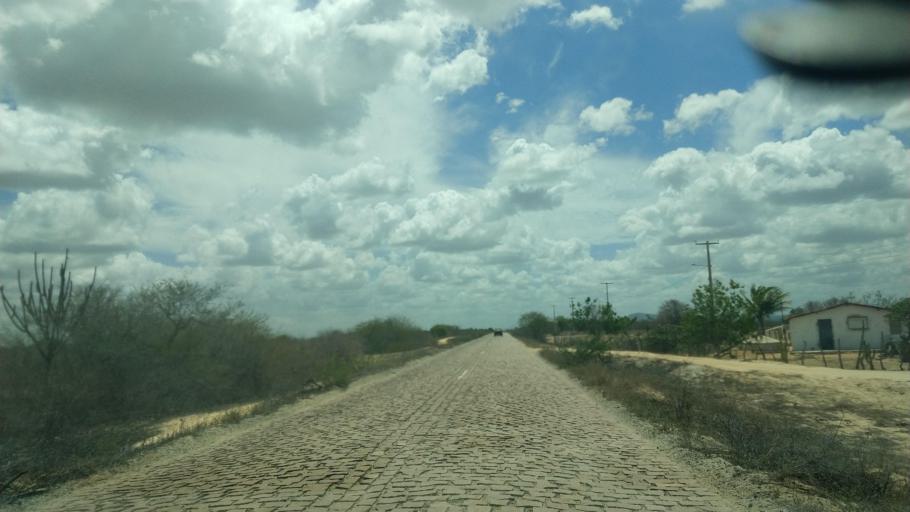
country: BR
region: Rio Grande do Norte
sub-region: Sao Paulo Do Potengi
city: Sao Paulo do Potengi
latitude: -5.9705
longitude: -35.8534
